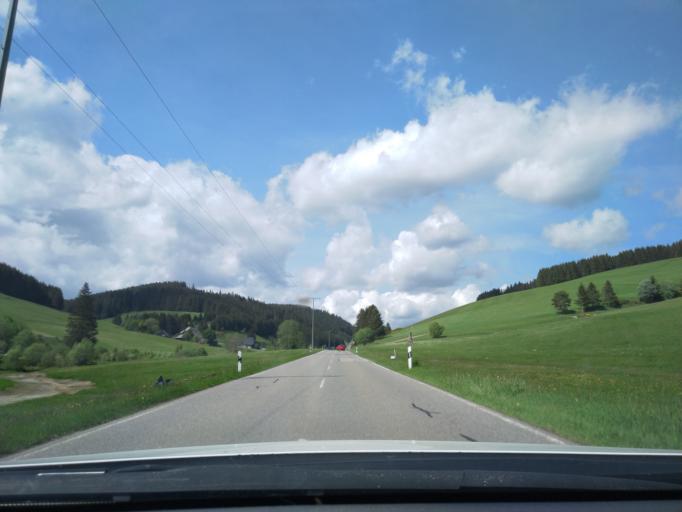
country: DE
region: Baden-Wuerttemberg
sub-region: Freiburg Region
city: Furtwangen im Schwarzwald
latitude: 48.0511
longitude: 8.2529
